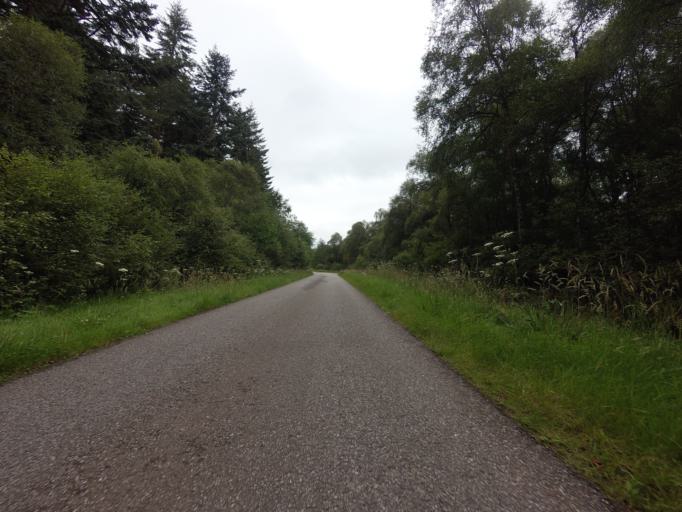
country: GB
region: Scotland
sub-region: Highland
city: Evanton
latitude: 57.9682
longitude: -4.4119
